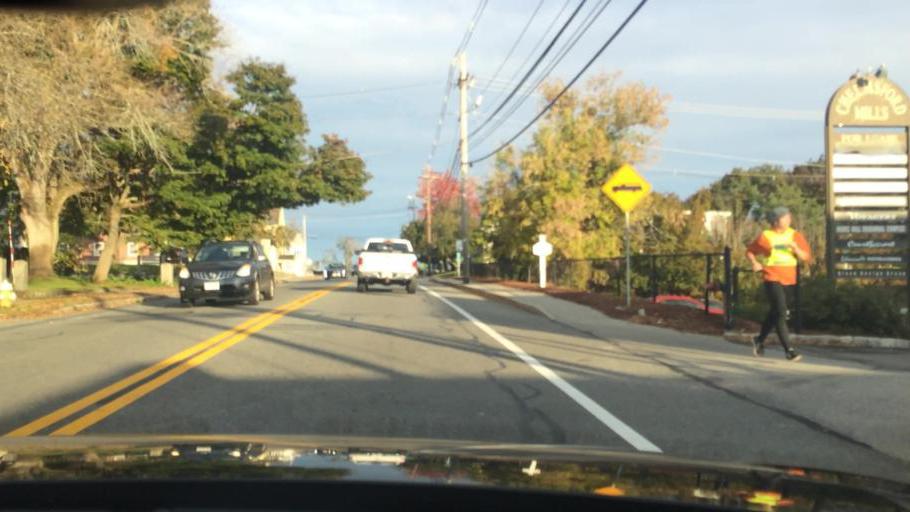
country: US
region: Massachusetts
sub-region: Middlesex County
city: Chelmsford
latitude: 42.6366
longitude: -71.3801
